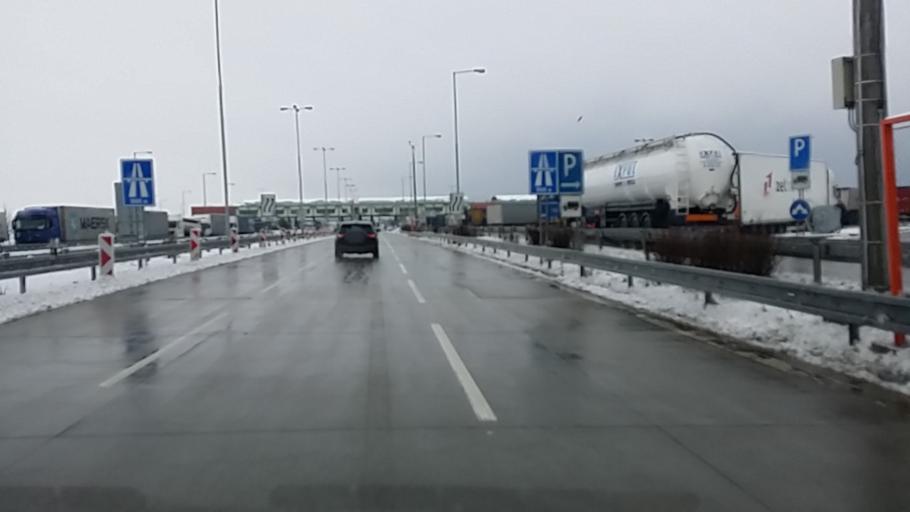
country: HU
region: Gyor-Moson-Sopron
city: Rajka
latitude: 48.0136
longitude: 17.1753
